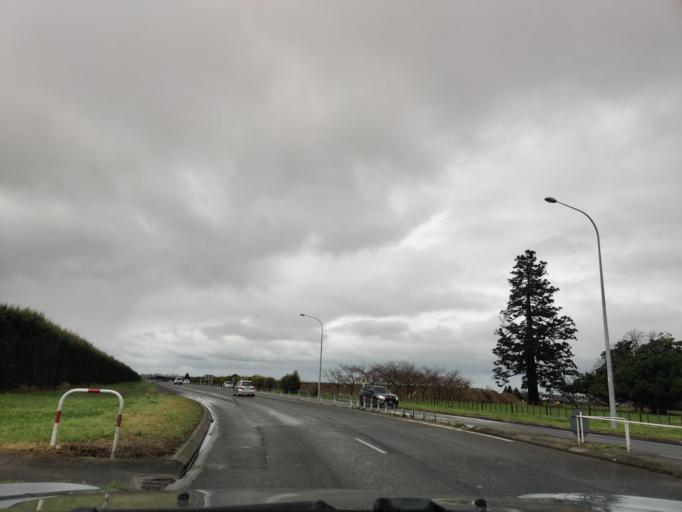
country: NZ
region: Hawke's Bay
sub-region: Hastings District
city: Hastings
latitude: -39.6198
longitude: 176.8169
